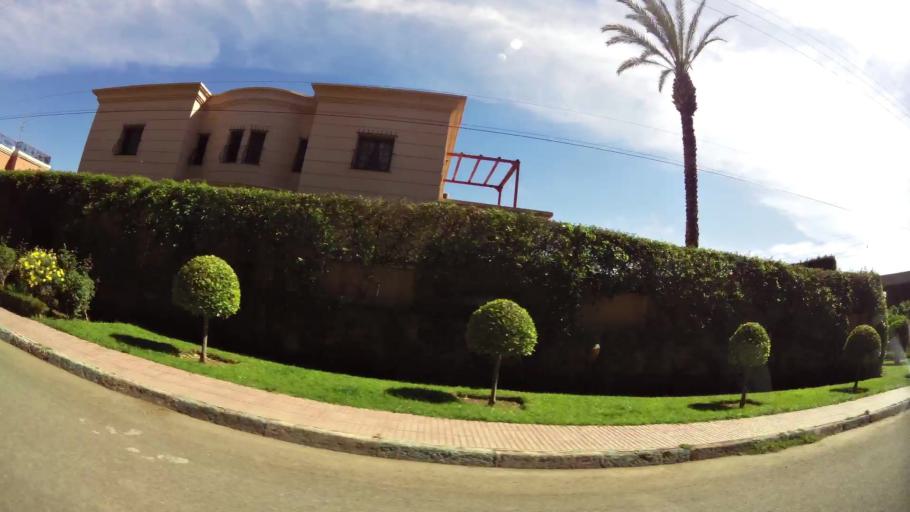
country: MA
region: Marrakech-Tensift-Al Haouz
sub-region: Marrakech
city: Marrakesh
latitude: 31.6450
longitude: -8.0491
